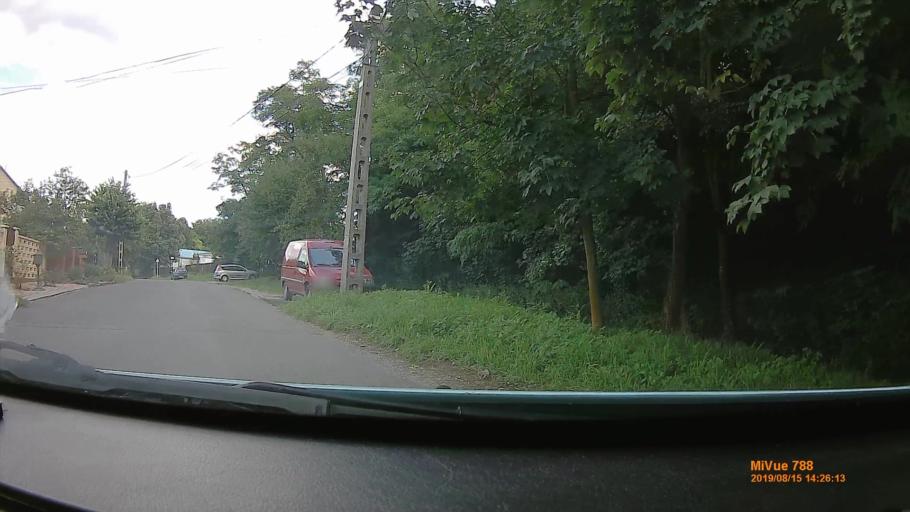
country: HU
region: Borsod-Abauj-Zemplen
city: Kazincbarcika
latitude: 48.2559
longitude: 20.6139
